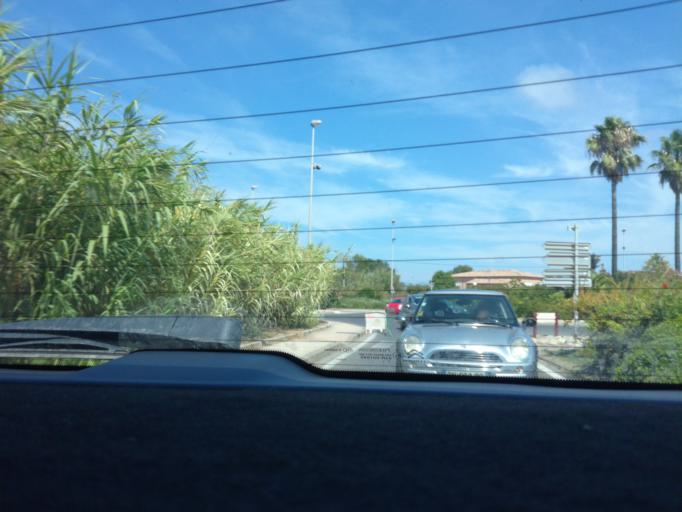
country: FR
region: Provence-Alpes-Cote d'Azur
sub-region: Departement du Var
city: Hyeres
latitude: 43.0404
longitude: 6.1452
